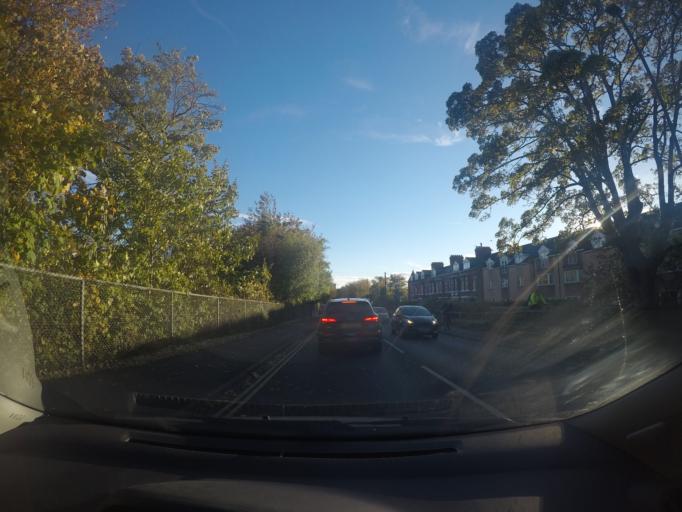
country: GB
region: England
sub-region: City of York
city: York
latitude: 53.9728
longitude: -1.0820
